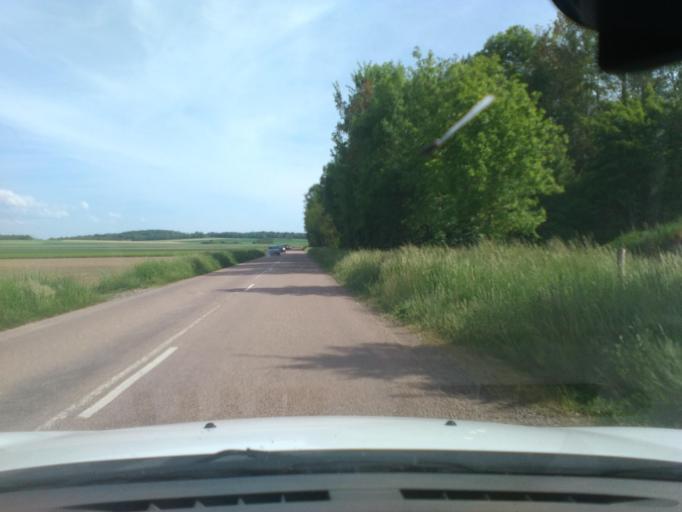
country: FR
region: Lorraine
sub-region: Departement des Vosges
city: Rambervillers
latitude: 48.4203
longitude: 6.5834
